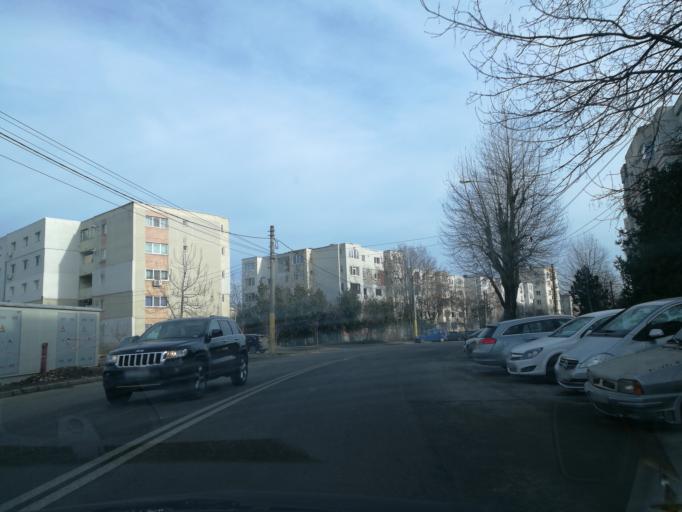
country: RO
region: Constanta
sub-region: Municipiul Constanta
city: Constanta
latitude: 44.1778
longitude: 28.6117
